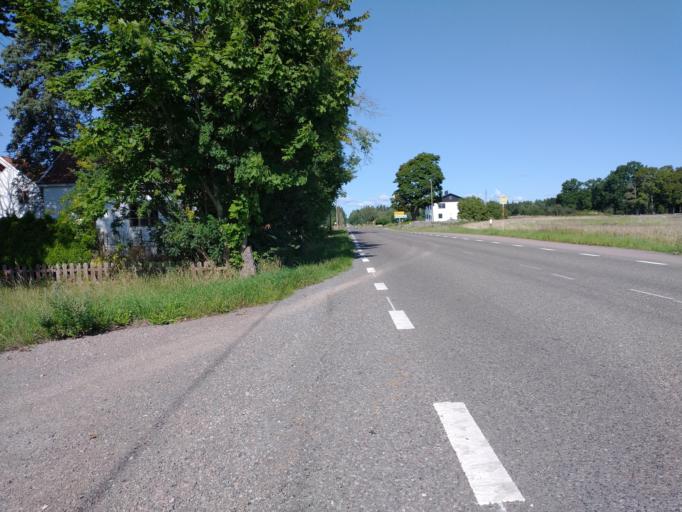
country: SE
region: Kalmar
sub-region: Kalmar Kommun
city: Lindsdal
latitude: 56.7919
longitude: 16.2548
